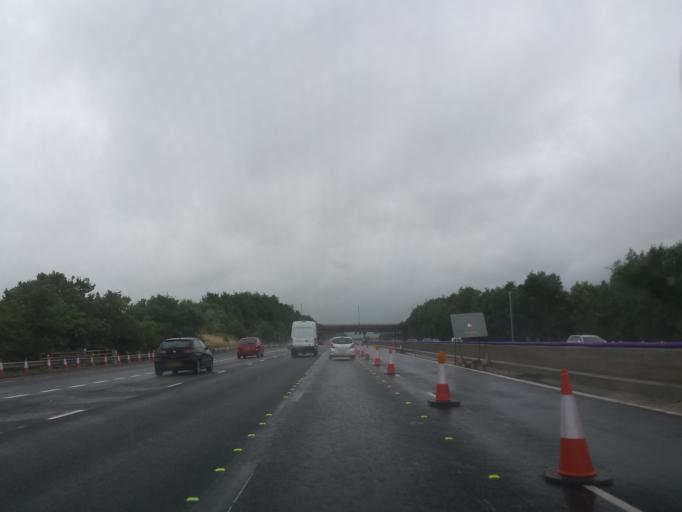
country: GB
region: England
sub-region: Derbyshire
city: Barlborough
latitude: 53.2832
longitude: -1.2973
